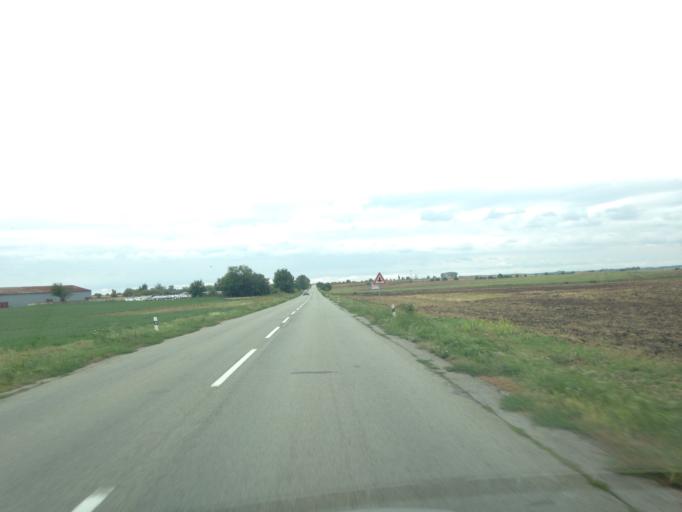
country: SK
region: Nitriansky
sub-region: Okres Komarno
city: Hurbanovo
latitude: 47.9061
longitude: 18.3340
